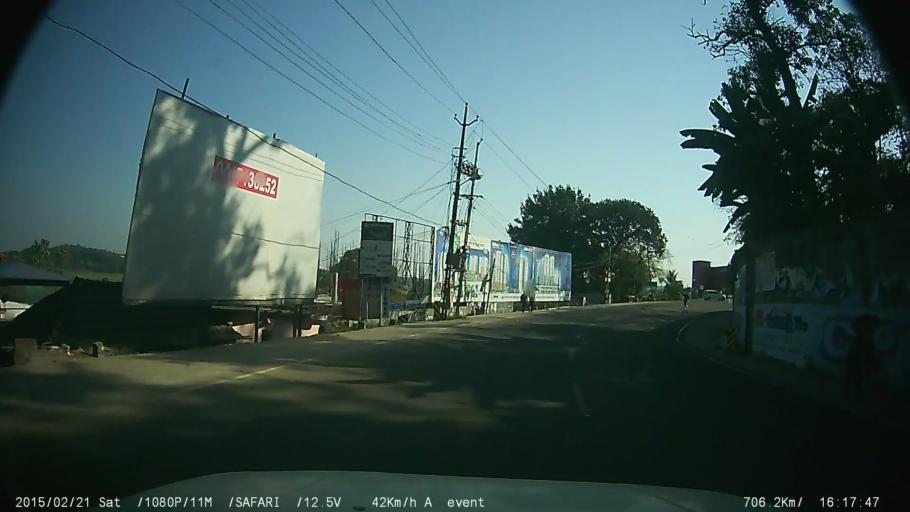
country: IN
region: Kerala
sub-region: Kottayam
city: Kottayam
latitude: 9.5823
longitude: 76.5233
